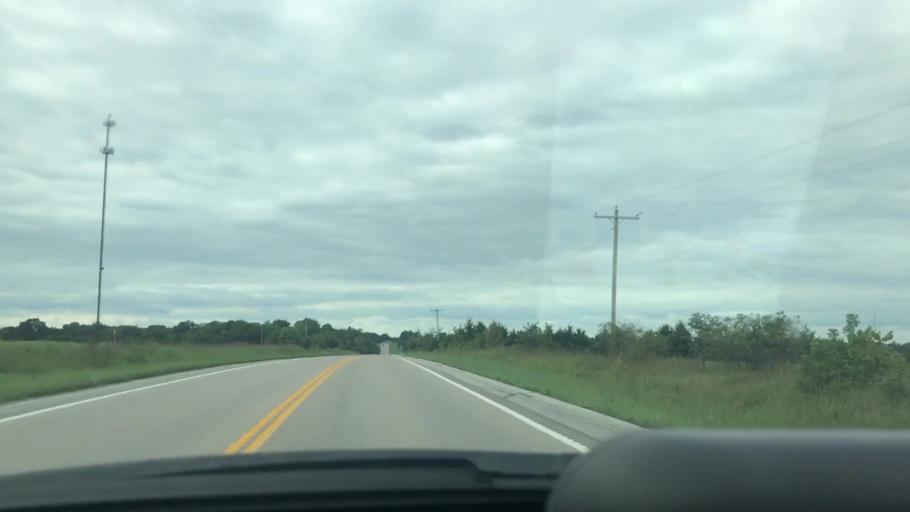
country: US
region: Missouri
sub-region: Benton County
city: Warsaw
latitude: 38.1440
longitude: -93.2895
